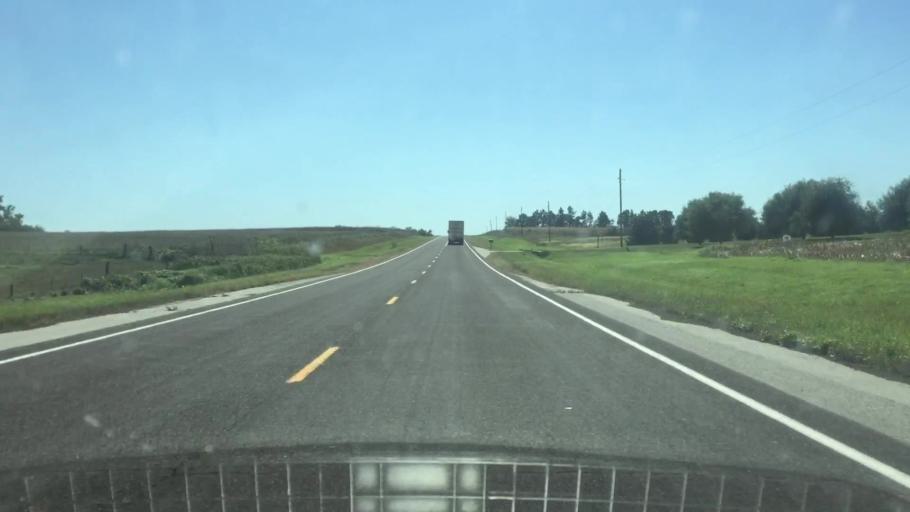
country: US
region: Nebraska
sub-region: Gage County
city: Wymore
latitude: 40.0292
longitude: -96.6523
